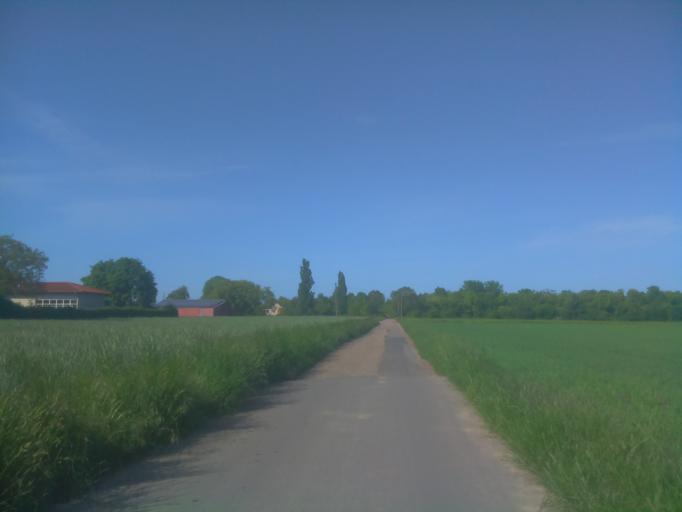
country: DE
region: Baden-Wuerttemberg
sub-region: Karlsruhe Region
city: Edingen-Neckarhausen
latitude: 49.4560
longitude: 8.5923
